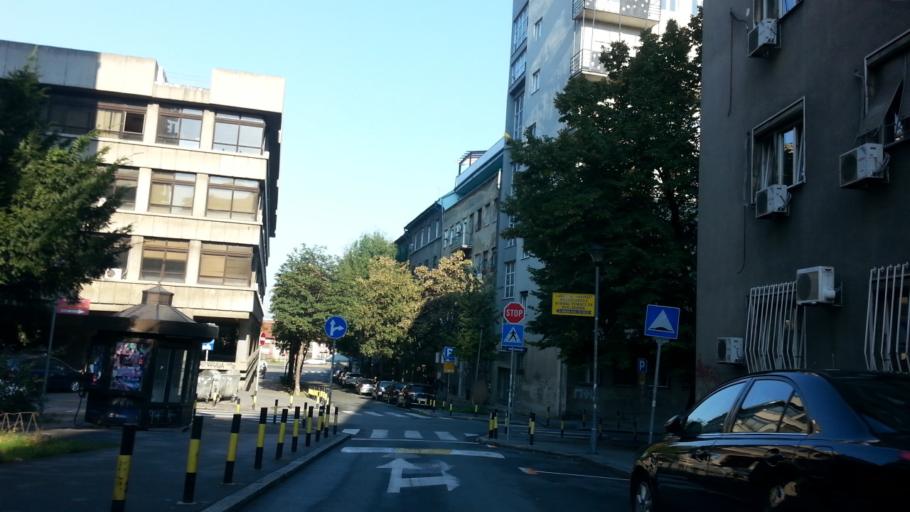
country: RS
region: Central Serbia
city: Belgrade
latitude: 44.8050
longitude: 20.4558
